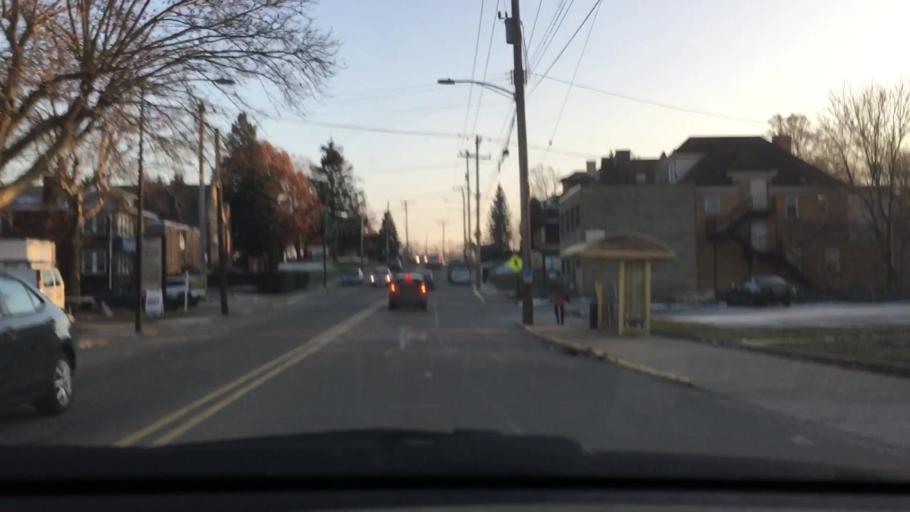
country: US
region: Pennsylvania
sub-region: Allegheny County
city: Brentwood
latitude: 40.3807
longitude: -79.9759
